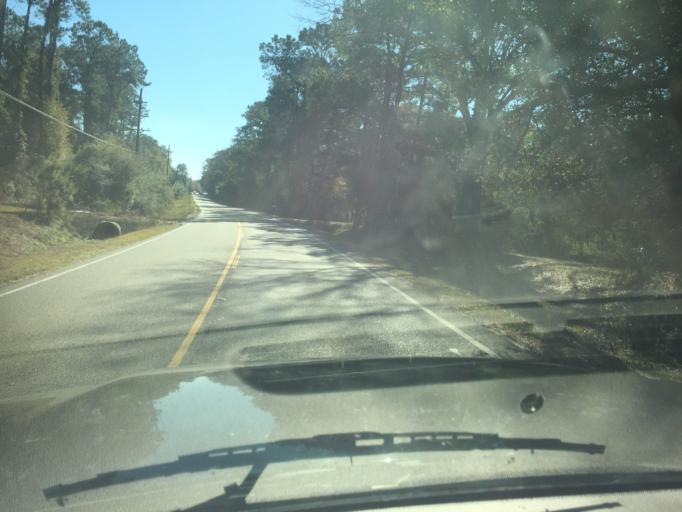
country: US
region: Louisiana
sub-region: Saint Tammany Parish
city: Slidell
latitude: 30.3079
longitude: -89.7292
